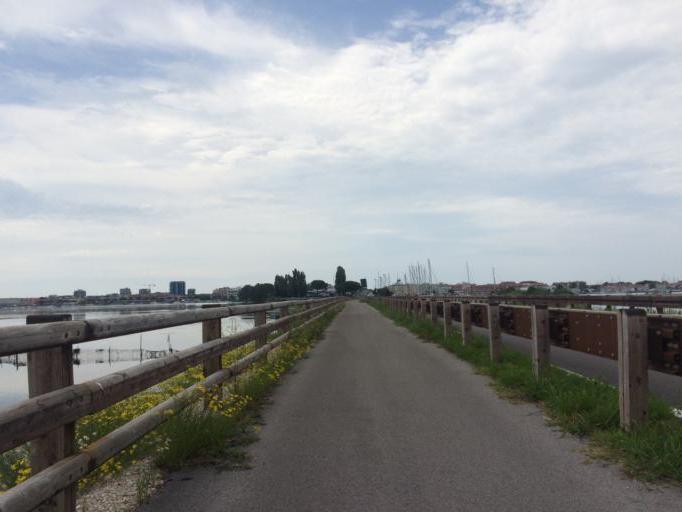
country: IT
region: Friuli Venezia Giulia
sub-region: Provincia di Gorizia
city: Grado
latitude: 45.6892
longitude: 13.3848
